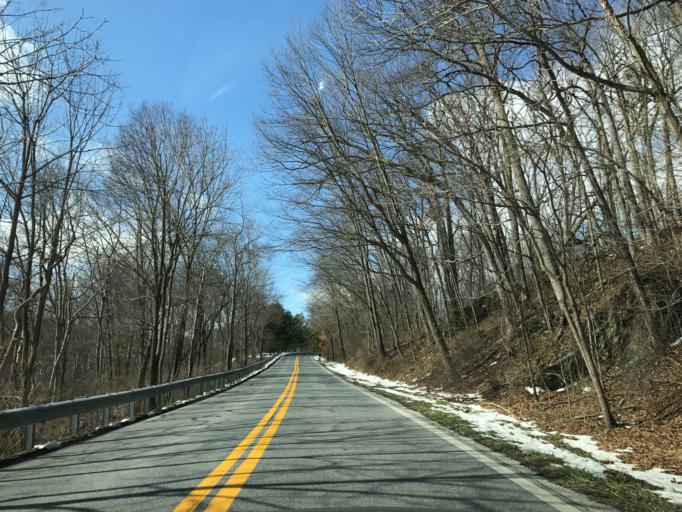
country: US
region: Maryland
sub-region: Carroll County
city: Hampstead
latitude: 39.6575
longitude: -76.8120
